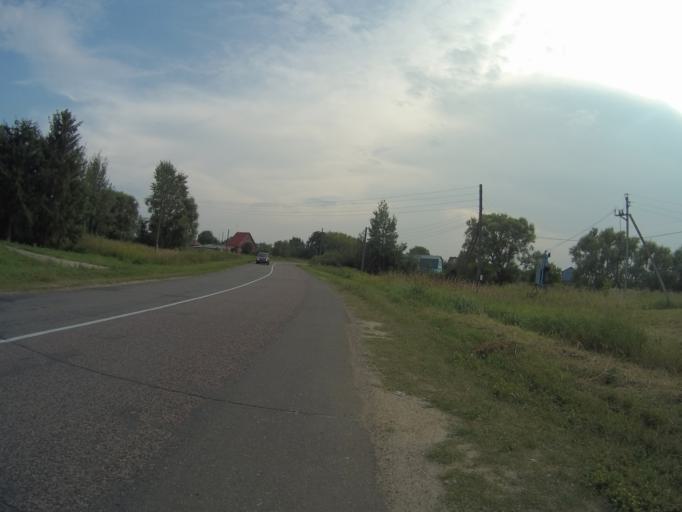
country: RU
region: Vladimir
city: Suzdal'
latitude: 56.4043
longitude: 40.3416
